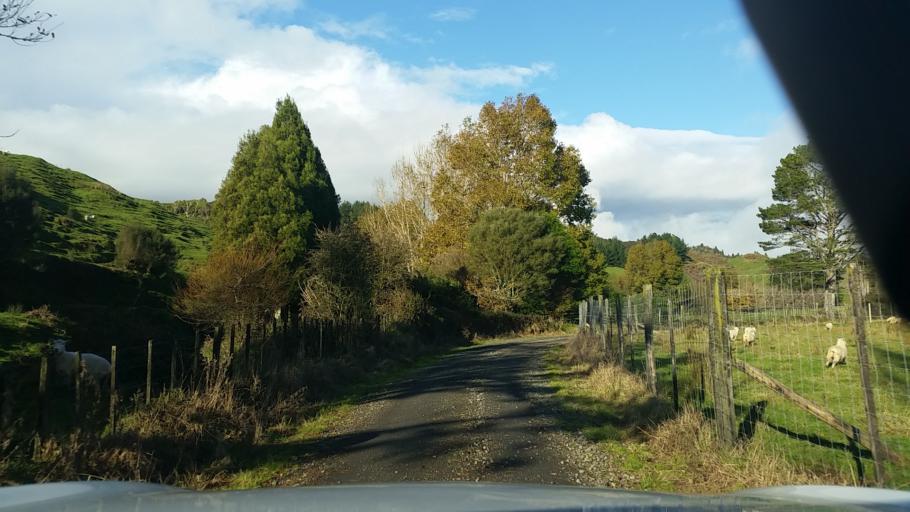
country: NZ
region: Taranaki
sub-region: New Plymouth District
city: Waitara
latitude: -39.1282
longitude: 174.4474
